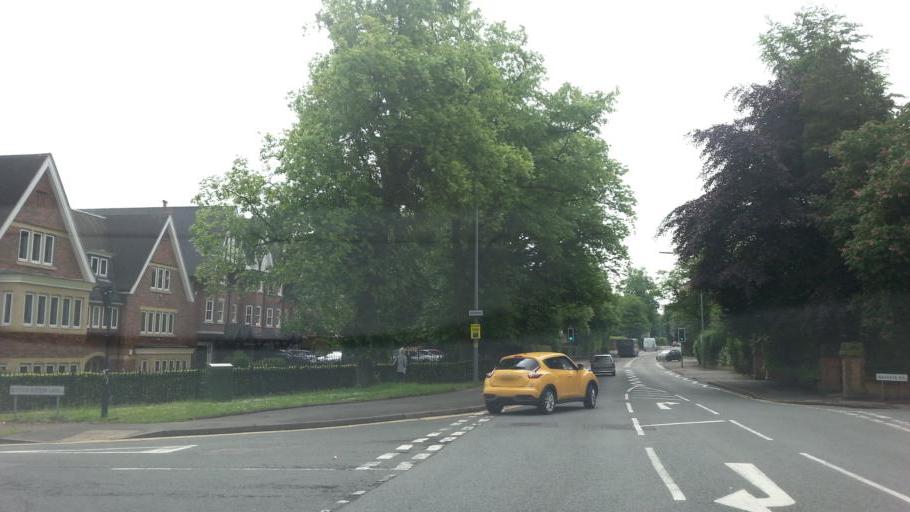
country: GB
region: England
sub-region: City and Borough of Birmingham
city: Sutton Coldfield
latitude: 52.5733
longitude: -1.8247
